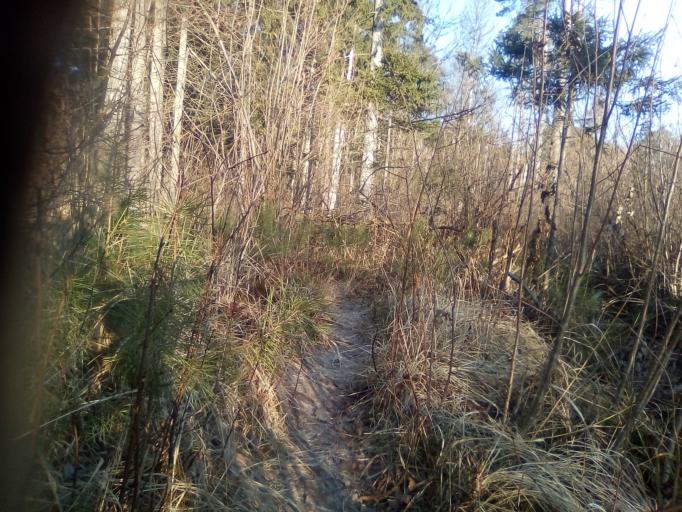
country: RU
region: Moskovskaya
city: Gorki Vtoryye
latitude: 55.6831
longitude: 37.1608
